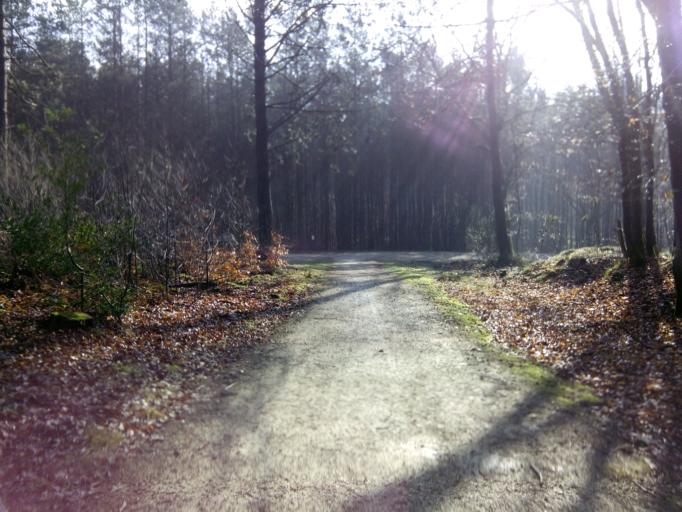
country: NL
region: Utrecht
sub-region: Gemeente Utrechtse Heuvelrug
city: Leersum
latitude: 52.0136
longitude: 5.4451
